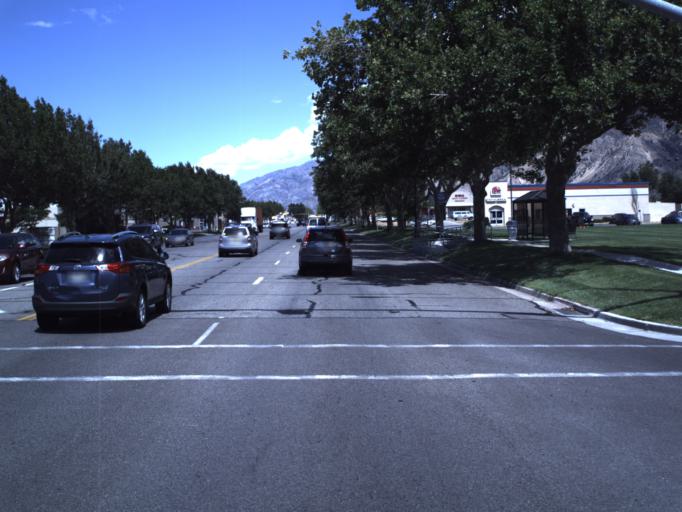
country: US
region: Utah
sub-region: Box Elder County
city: Brigham City
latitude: 41.4901
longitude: -112.0161
